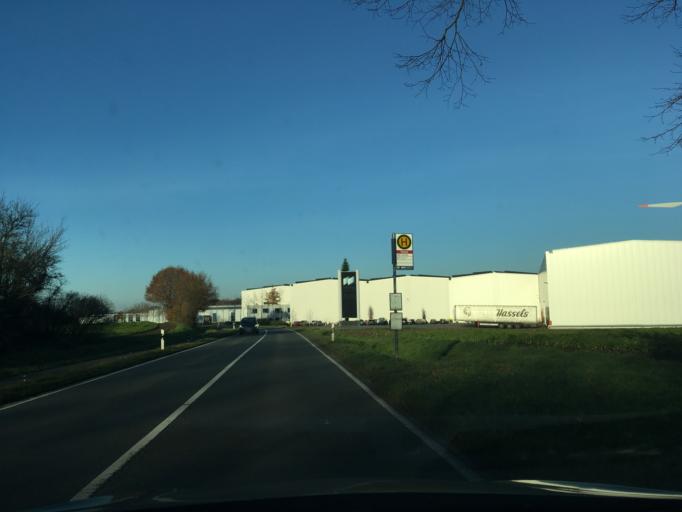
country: DE
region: North Rhine-Westphalia
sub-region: Regierungsbezirk Munster
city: Ahaus
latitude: 52.1037
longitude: 6.9634
